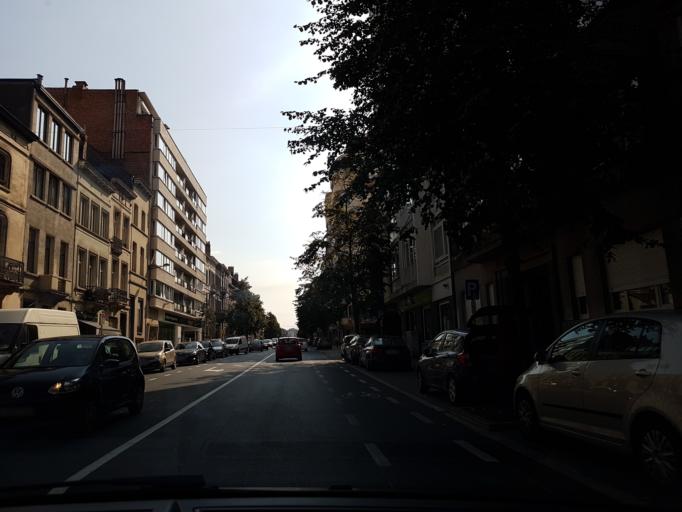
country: BE
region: Brussels Capital
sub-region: Bruxelles-Capitale
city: Brussels
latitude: 50.8394
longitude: 4.3855
